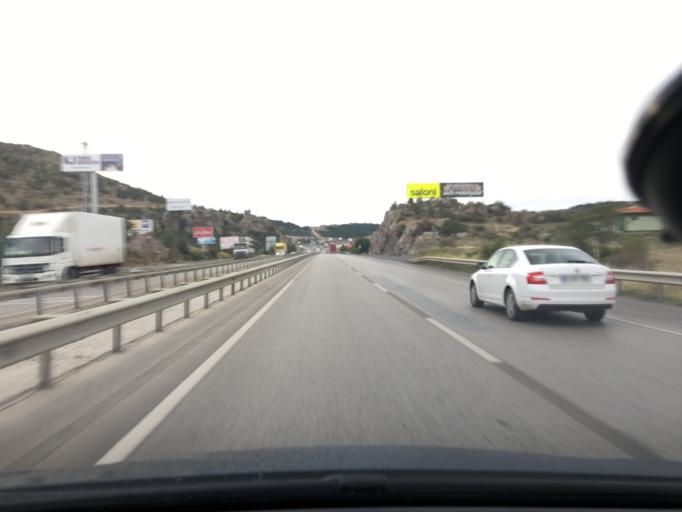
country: TR
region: Afyonkarahisar
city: Afyonkarahisar
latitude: 38.7927
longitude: 30.4490
